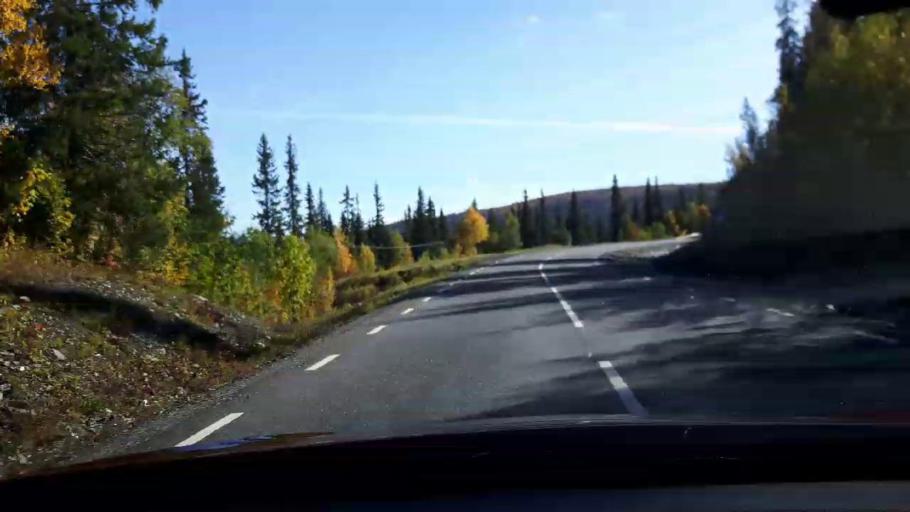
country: NO
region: Nord-Trondelag
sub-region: Royrvik
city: Royrvik
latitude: 64.8570
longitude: 14.1805
